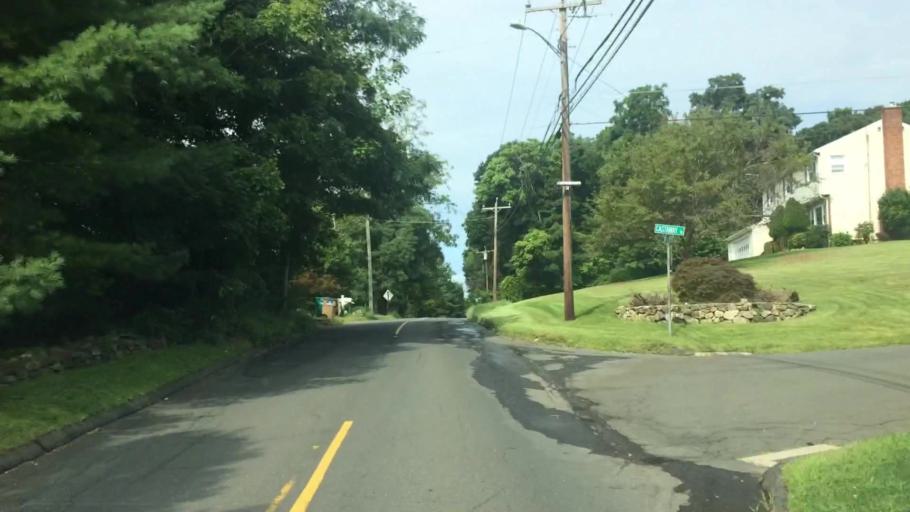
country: US
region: Connecticut
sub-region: Fairfield County
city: Danbury
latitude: 41.4054
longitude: -73.4942
